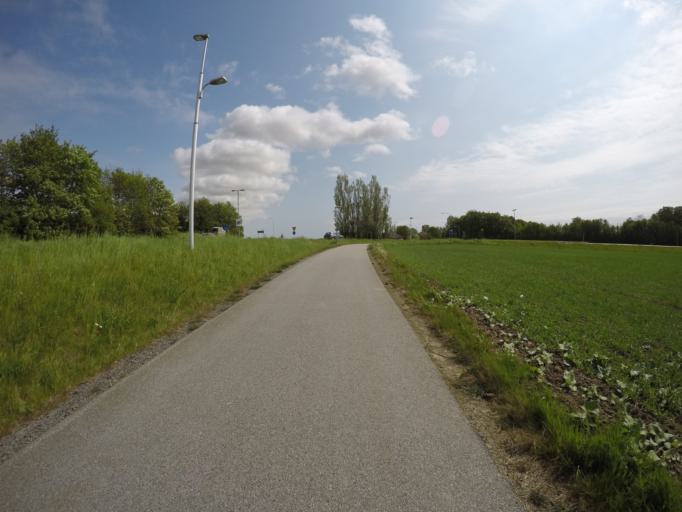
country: SE
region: Skane
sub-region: Malmo
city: Tygelsjo
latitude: 55.5314
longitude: 12.9948
